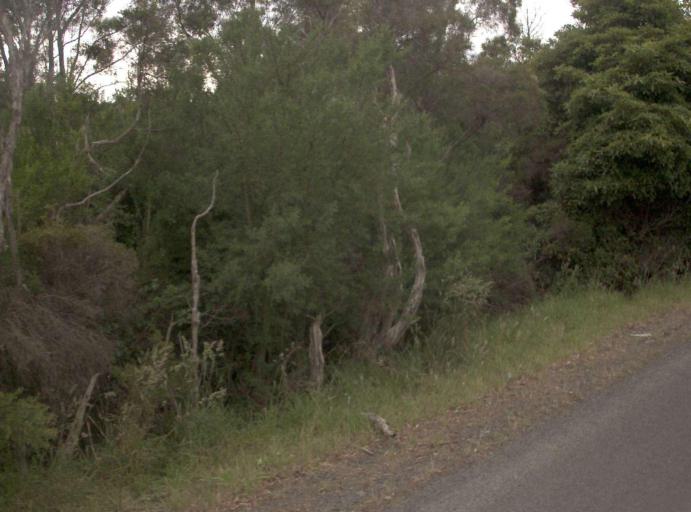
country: AU
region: Victoria
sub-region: Latrobe
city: Traralgon
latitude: -38.5477
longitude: 146.6936
